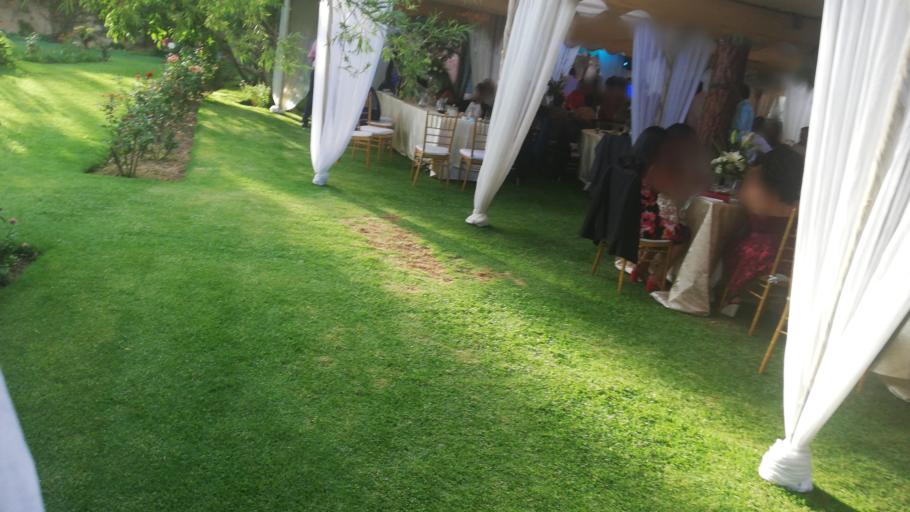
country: BO
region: Cochabamba
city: Cochabamba
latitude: -17.3354
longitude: -66.2405
